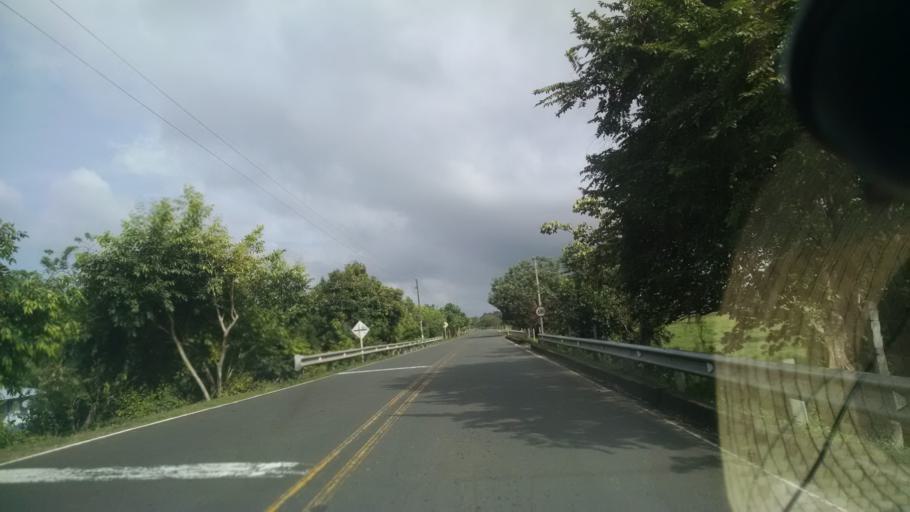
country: CO
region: Antioquia
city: Necocli
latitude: 8.6329
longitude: -76.7136
